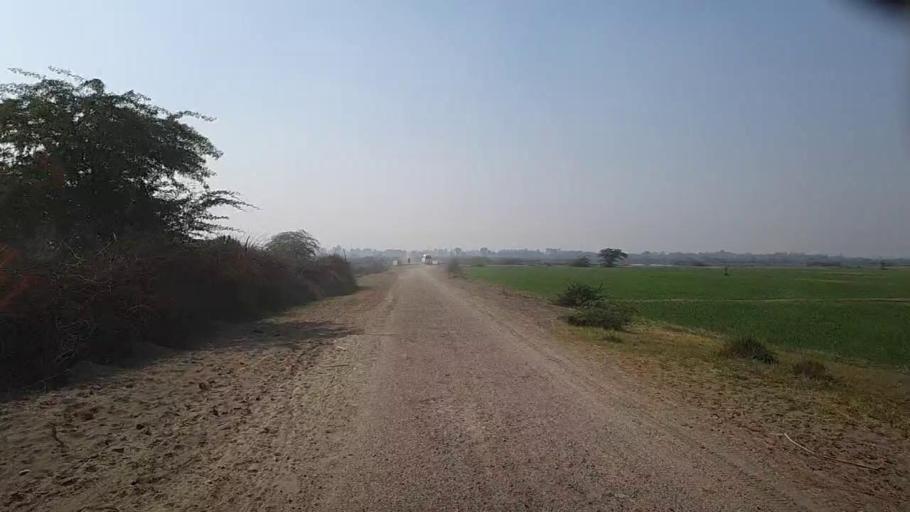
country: PK
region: Sindh
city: Bozdar
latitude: 27.2545
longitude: 68.6137
